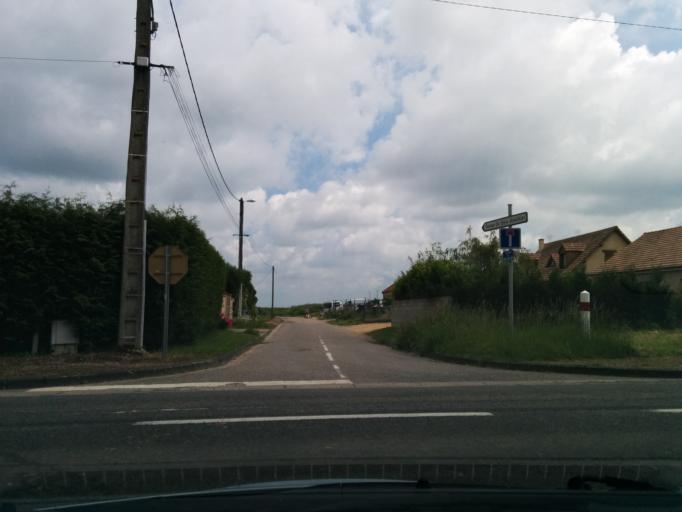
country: FR
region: Haute-Normandie
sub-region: Departement de l'Eure
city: Gasny
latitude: 49.1615
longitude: 1.5501
